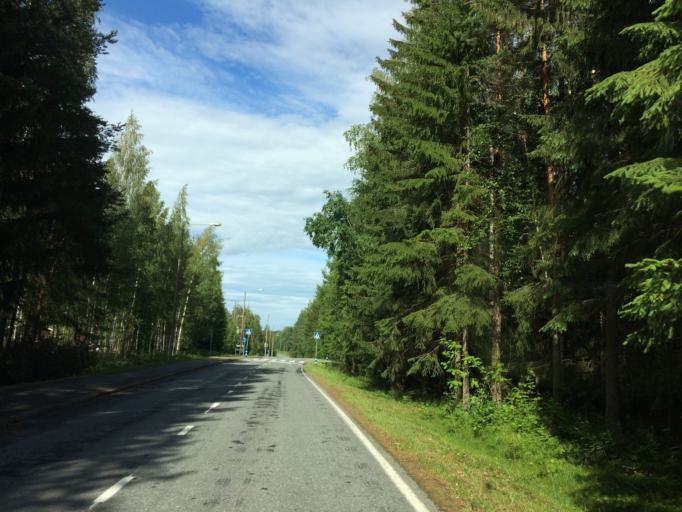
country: FI
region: Haeme
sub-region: Haemeenlinna
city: Janakkala
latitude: 60.9022
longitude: 24.6047
